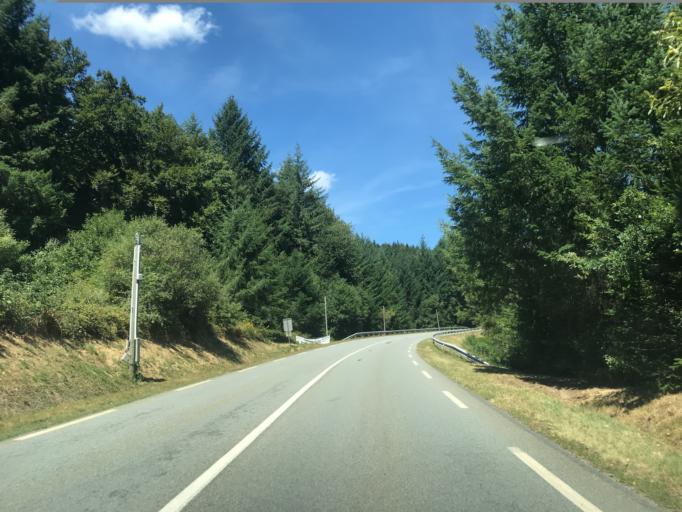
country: FR
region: Limousin
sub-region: Departement de la Correze
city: Meymac
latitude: 45.5486
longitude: 2.1456
